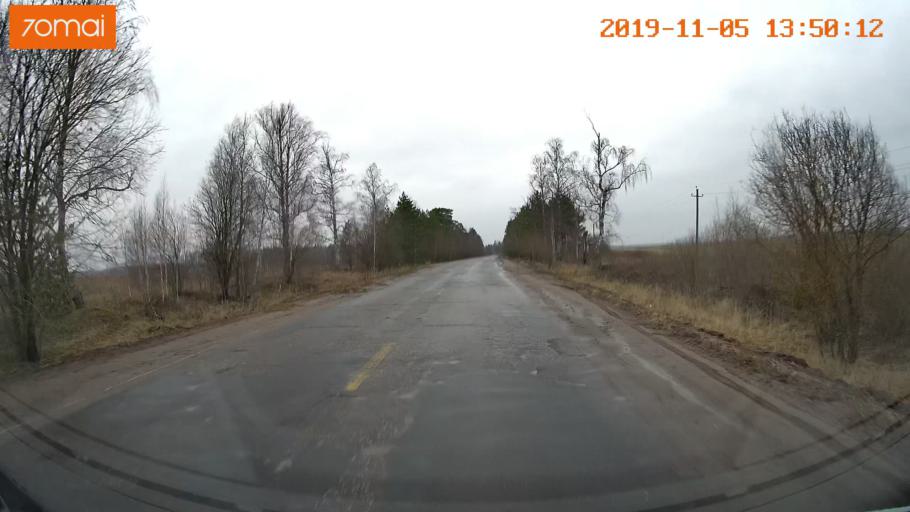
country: RU
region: Ivanovo
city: Kaminskiy
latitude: 57.0175
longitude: 41.4092
